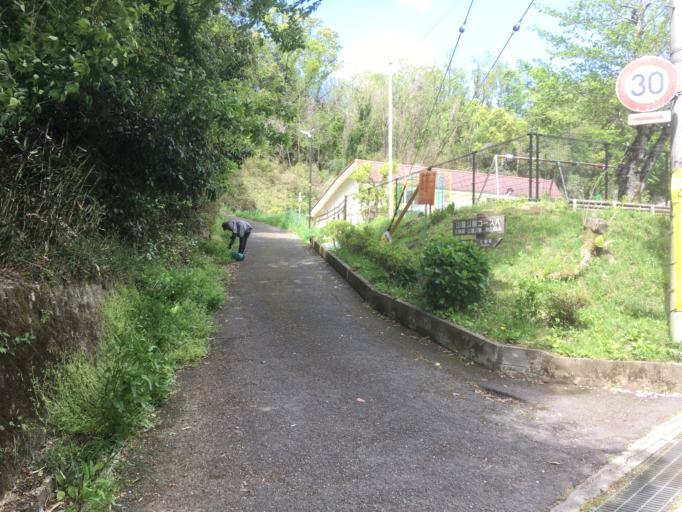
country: JP
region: Nara
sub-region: Ikoma-shi
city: Ikoma
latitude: 34.7045
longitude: 135.6894
